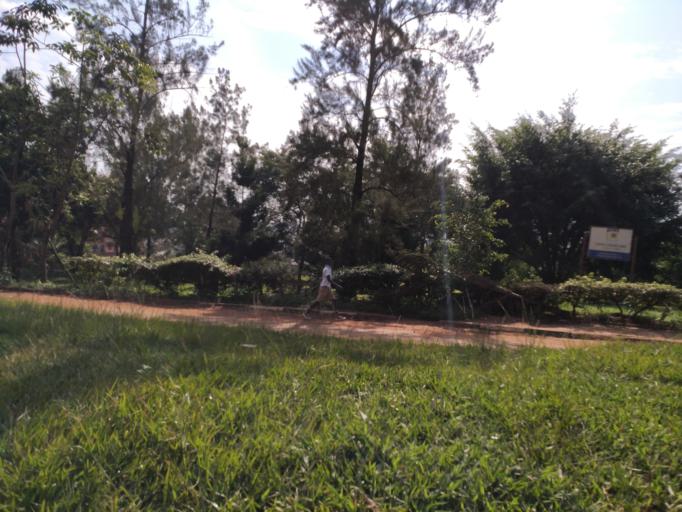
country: UG
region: Central Region
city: Kampala Central Division
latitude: 0.3372
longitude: 32.5699
